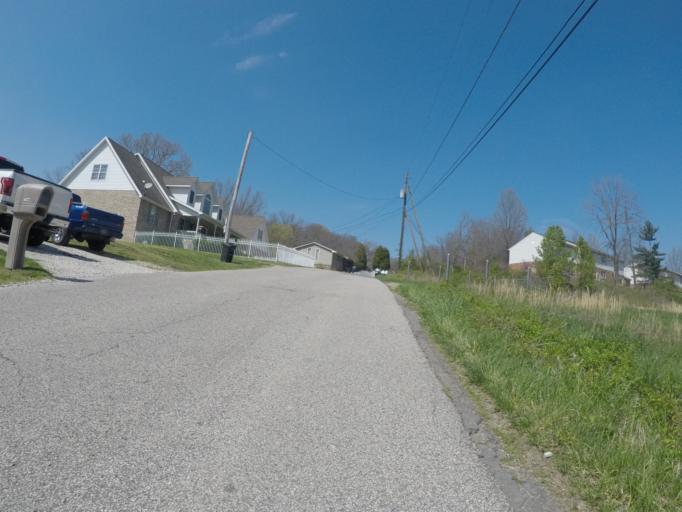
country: US
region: Ohio
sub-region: Lawrence County
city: Burlington
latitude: 38.3774
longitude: -82.5321
